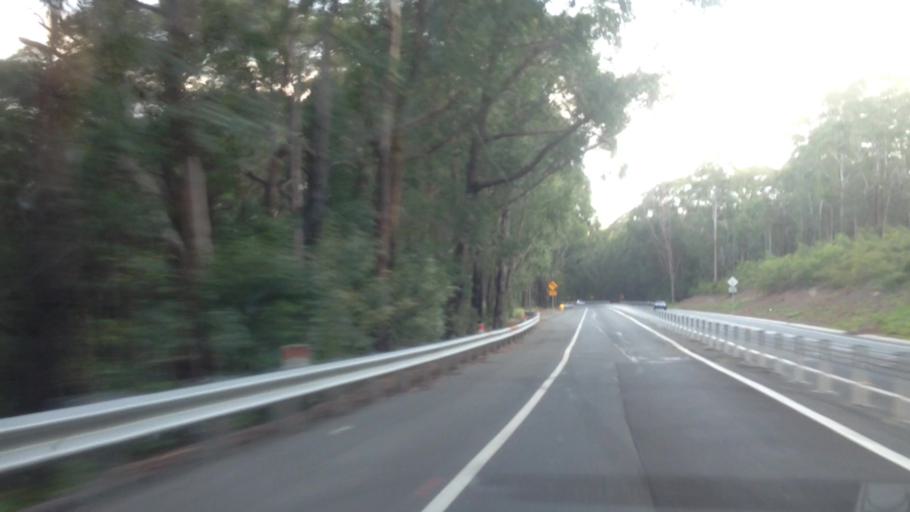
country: AU
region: New South Wales
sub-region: Lake Macquarie Shire
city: Cooranbong
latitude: -32.9716
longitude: 151.4822
